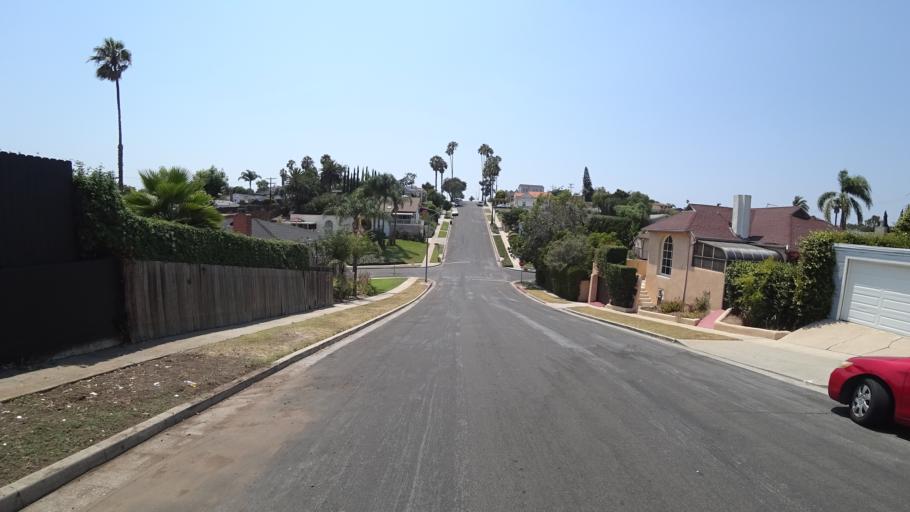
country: US
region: California
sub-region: Los Angeles County
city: View Park-Windsor Hills
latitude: 33.9826
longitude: -118.3453
